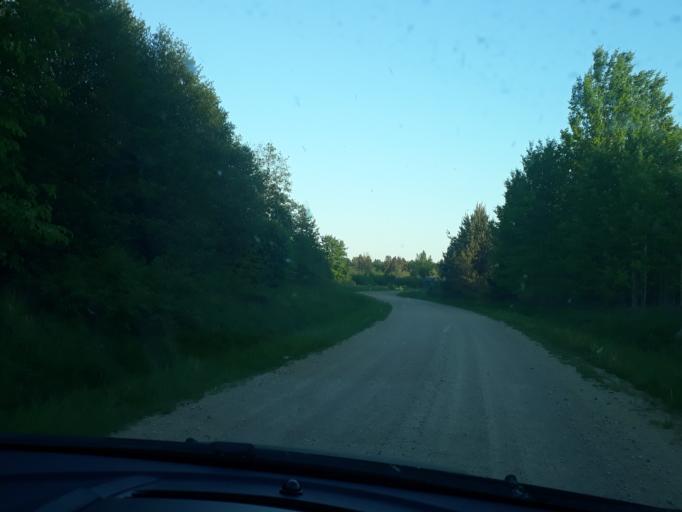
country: EE
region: Paernumaa
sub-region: Vaendra vald (alev)
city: Vandra
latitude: 58.5633
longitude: 24.9520
